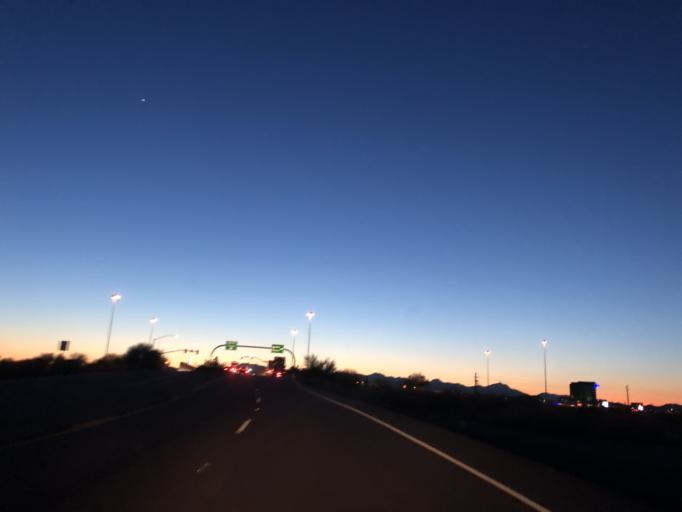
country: US
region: Arizona
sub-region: Maricopa County
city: Guadalupe
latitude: 33.2807
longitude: -111.9642
